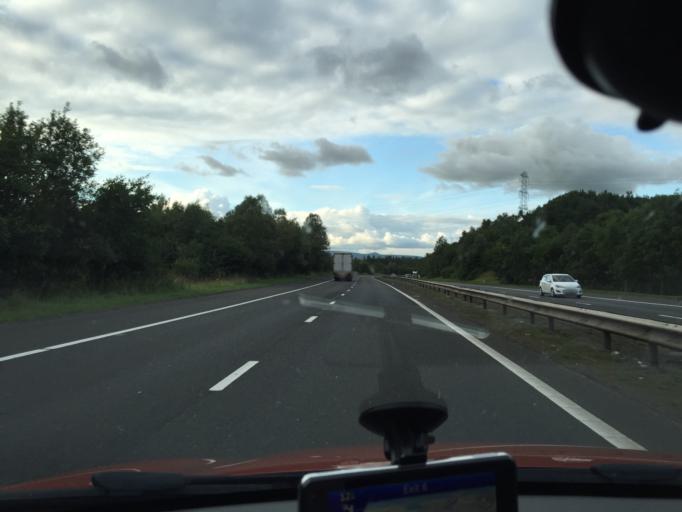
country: GB
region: Scotland
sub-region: North Lanarkshire
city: Chryston
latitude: 55.8775
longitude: -4.0803
